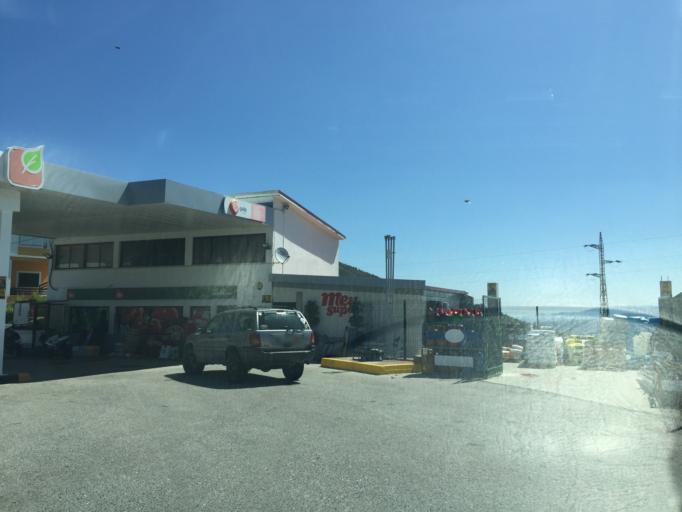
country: PT
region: Coimbra
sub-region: Pampilhosa da Serra
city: Pampilhosa da Serra
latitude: 40.1241
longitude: -7.8008
